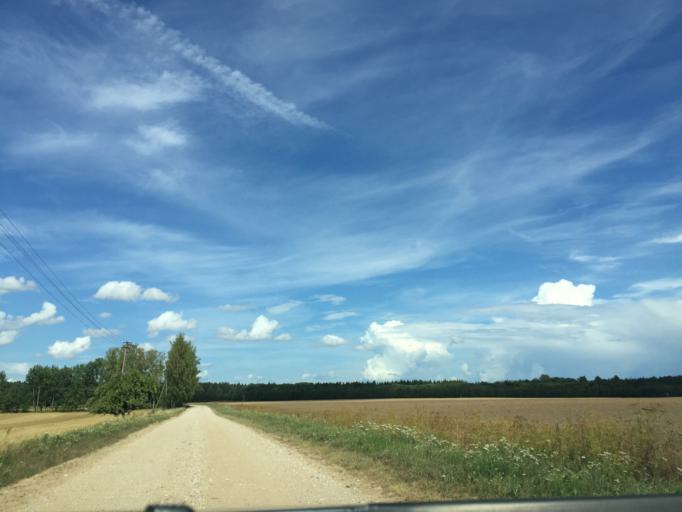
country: LT
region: Siauliu apskritis
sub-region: Joniskis
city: Joniskis
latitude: 56.3529
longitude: 23.6293
